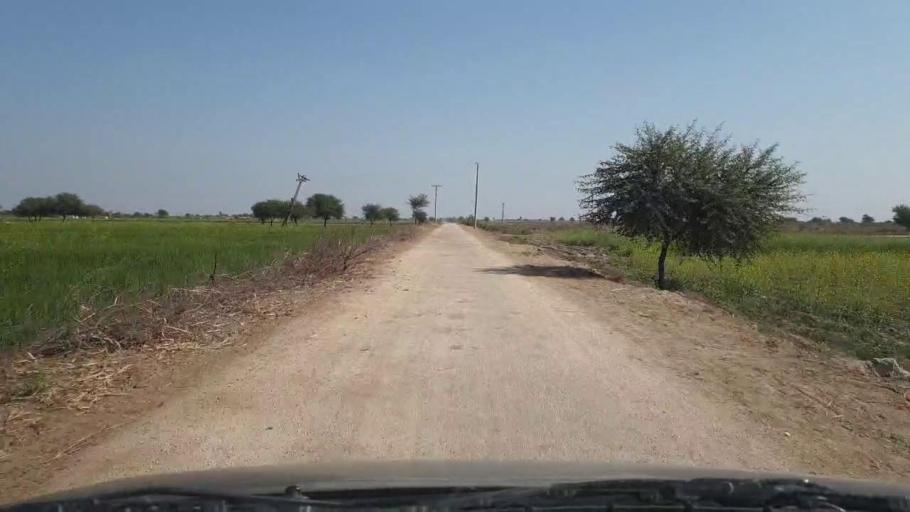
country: PK
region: Sindh
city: Samaro
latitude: 25.1998
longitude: 69.2897
